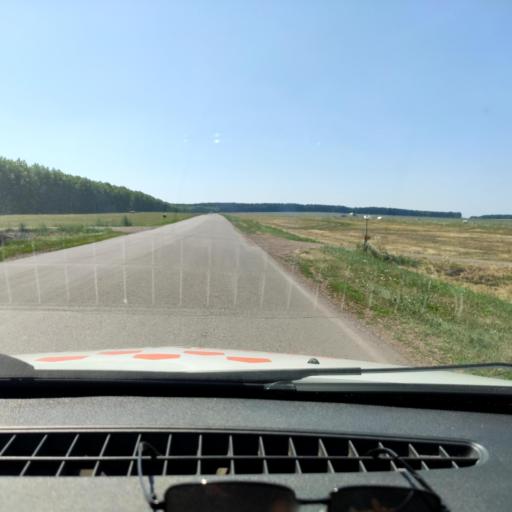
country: RU
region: Bashkortostan
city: Karmaskaly
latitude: 54.3465
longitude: 56.1121
